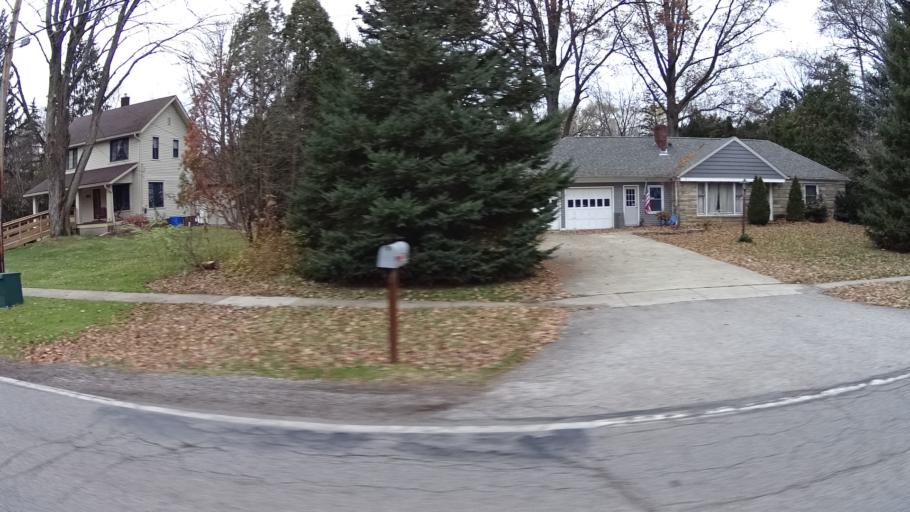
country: US
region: Ohio
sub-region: Lorain County
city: North Ridgeville
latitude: 41.3877
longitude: -82.0115
